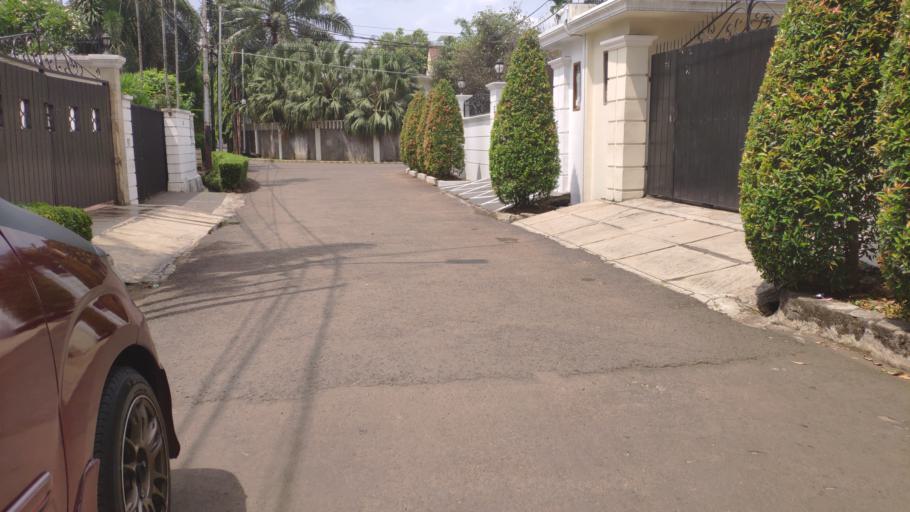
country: ID
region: Jakarta Raya
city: Jakarta
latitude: -6.2637
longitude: 106.8251
